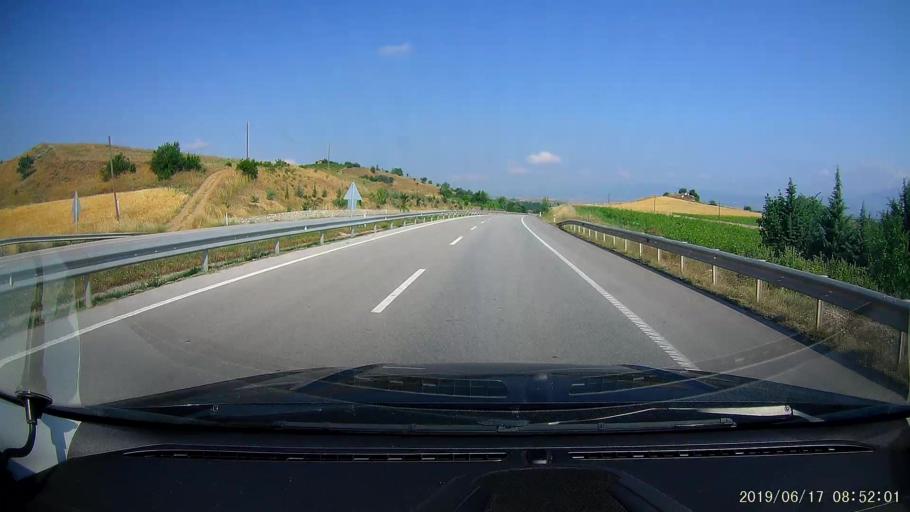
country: TR
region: Tokat
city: Erbaa
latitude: 40.6924
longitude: 36.5040
